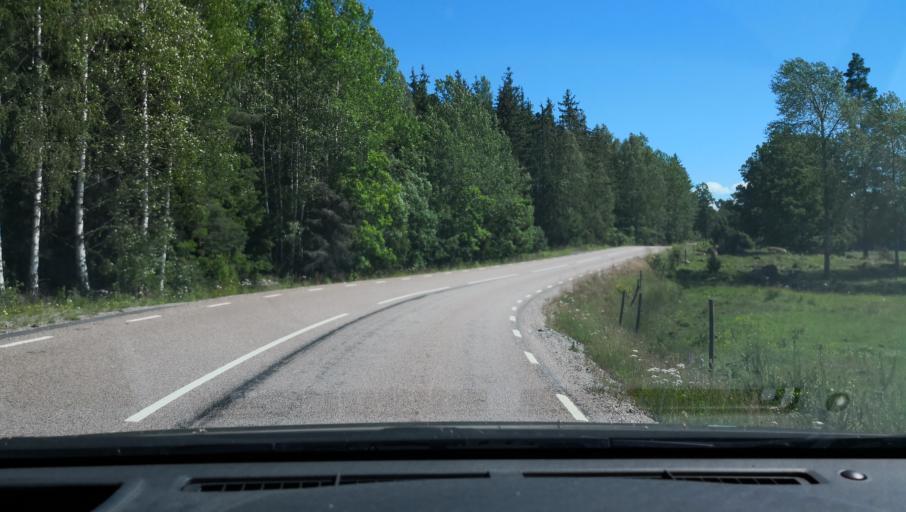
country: SE
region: Vaestmanland
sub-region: Arboga Kommun
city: Tyringe
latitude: 59.3021
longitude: 16.0181
